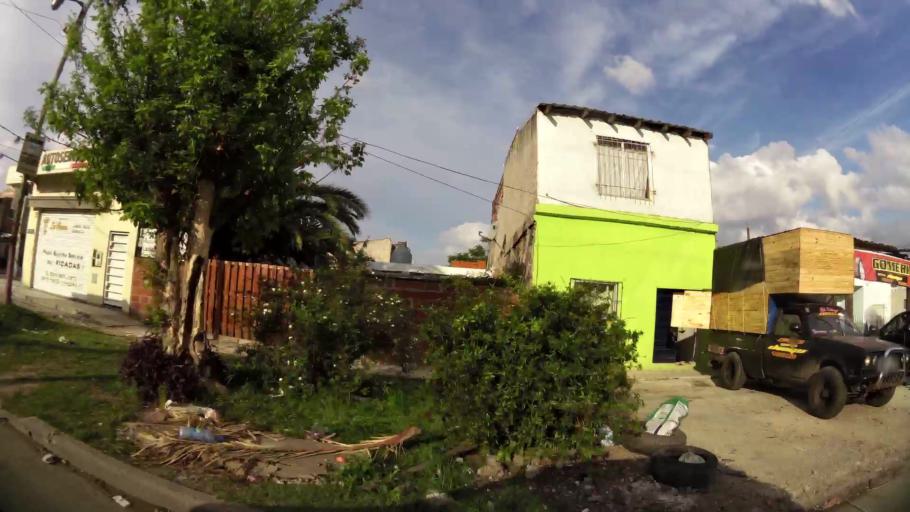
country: AR
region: Buenos Aires
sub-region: Partido de Quilmes
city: Quilmes
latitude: -34.7456
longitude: -58.2655
